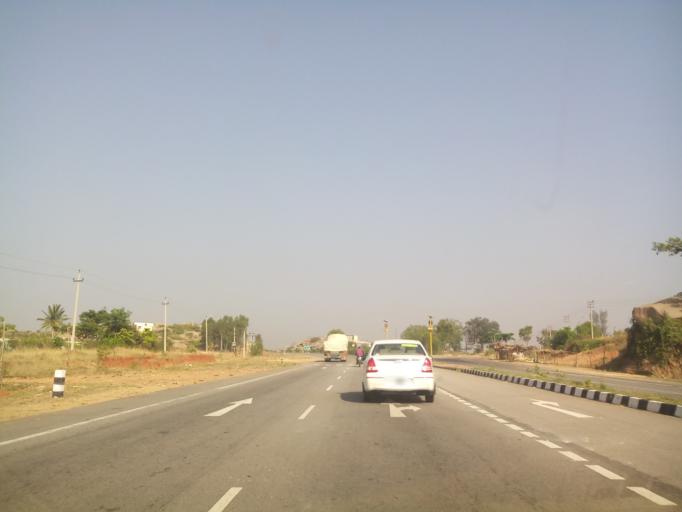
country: IN
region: Karnataka
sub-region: Bangalore Rural
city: Nelamangala
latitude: 13.0646
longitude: 77.2899
